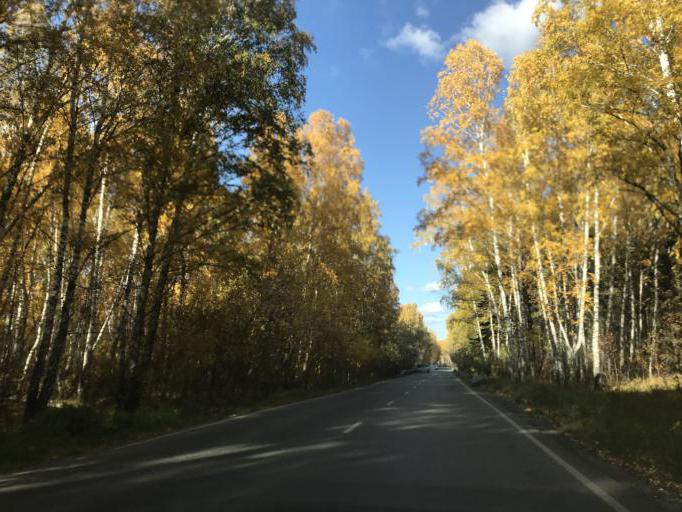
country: RU
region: Chelyabinsk
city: Dolgoderevenskoye
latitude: 55.2667
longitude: 61.3647
